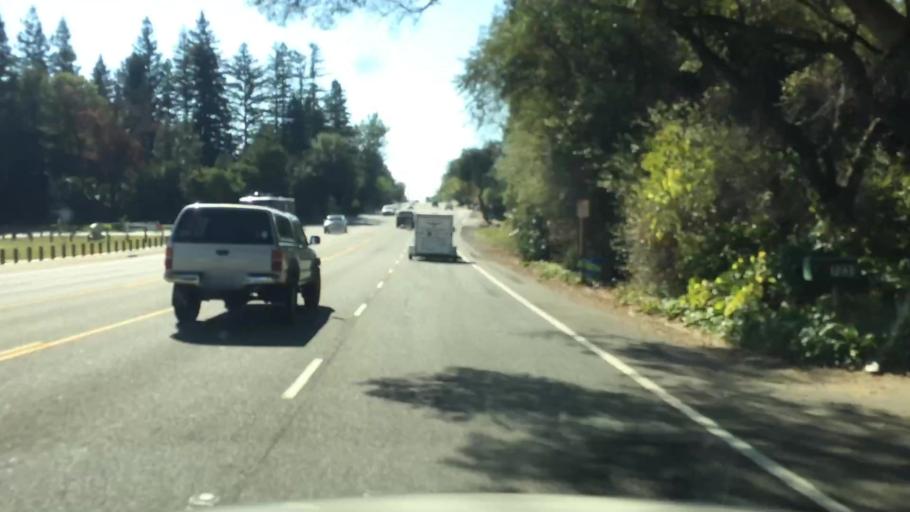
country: US
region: California
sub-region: Sacramento County
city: Orangevale
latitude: 38.6971
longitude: -121.2253
